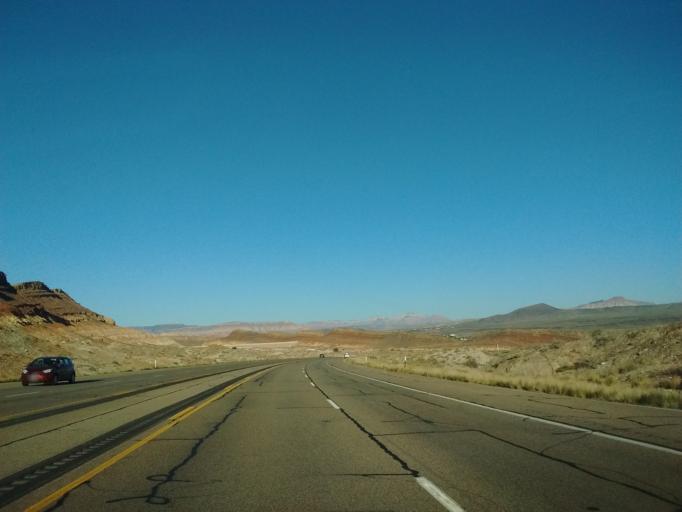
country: US
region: Utah
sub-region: Washington County
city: Washington
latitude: 37.1673
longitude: -113.4168
